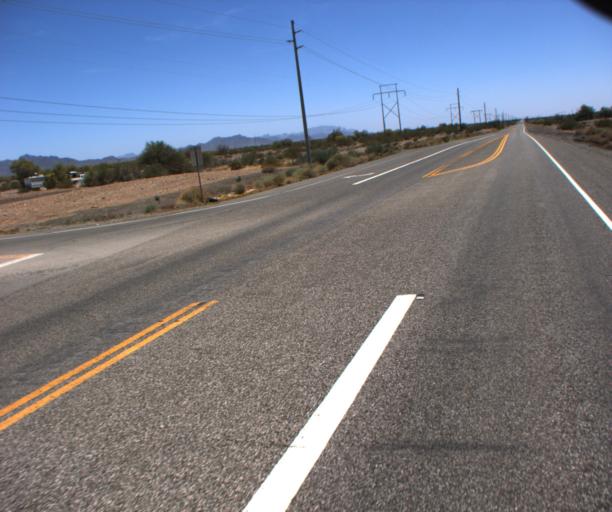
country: US
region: Arizona
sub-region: La Paz County
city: Quartzsite
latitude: 33.7097
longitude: -114.2171
